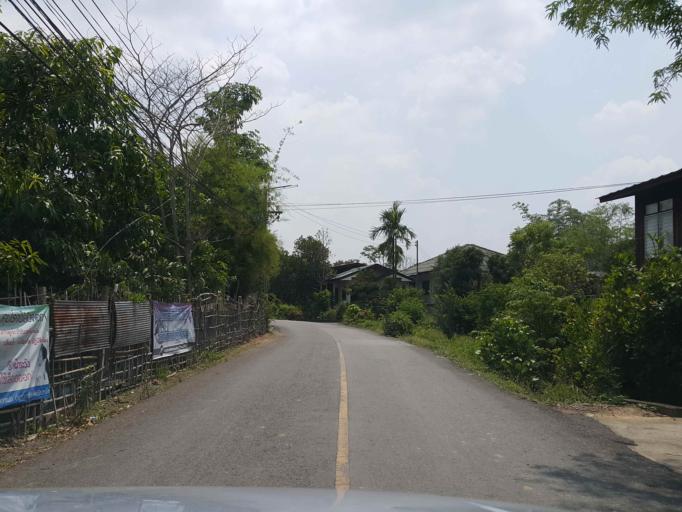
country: TH
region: Chiang Mai
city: Saraphi
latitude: 18.6771
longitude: 99.0258
